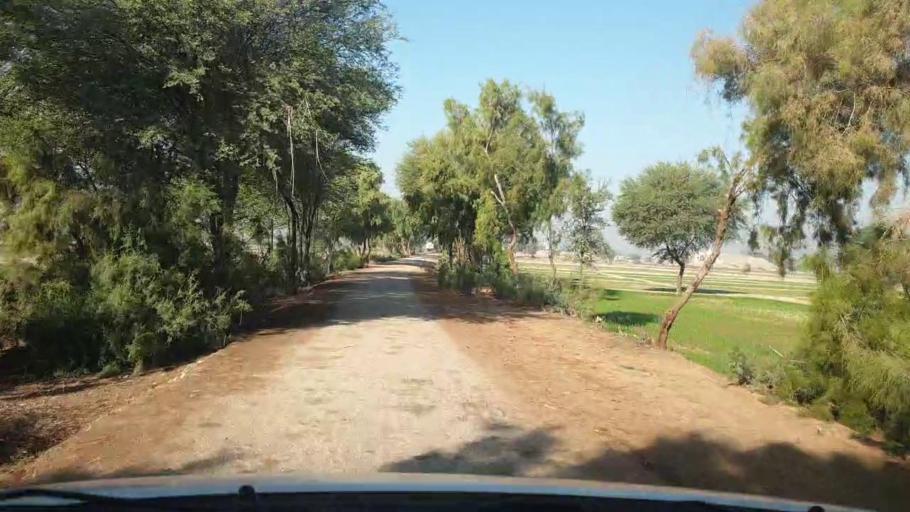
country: PK
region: Sindh
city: Dadu
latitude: 26.6751
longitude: 67.8374
